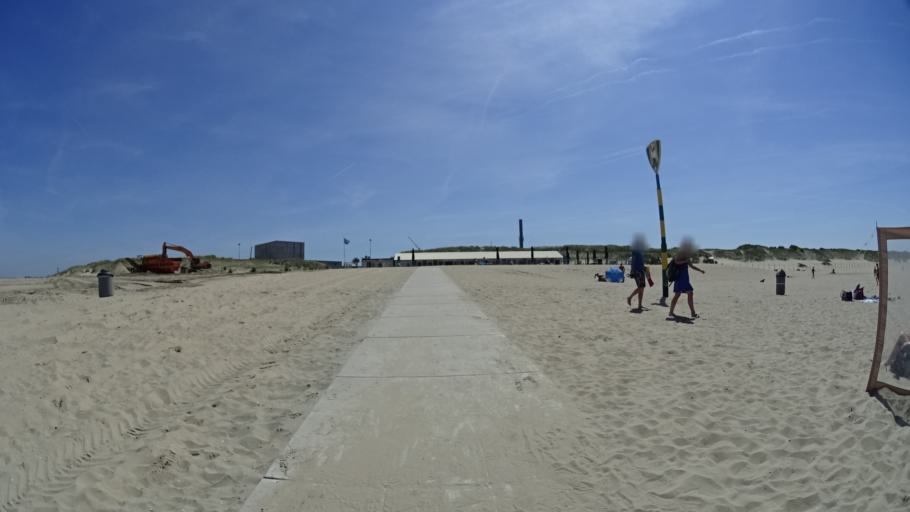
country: NL
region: South Holland
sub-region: Gemeente Den Haag
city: Scheveningen
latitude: 52.0978
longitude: 4.2551
